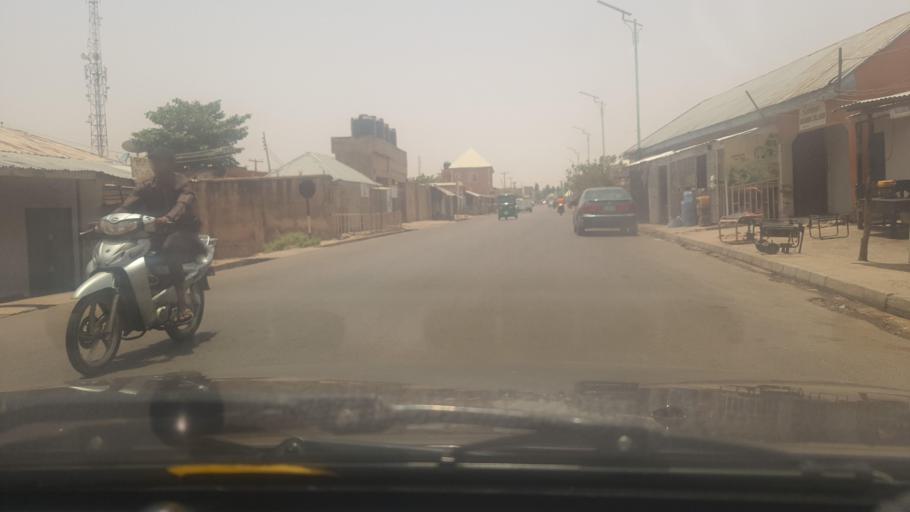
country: NG
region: Gombe
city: Gombe
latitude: 10.2988
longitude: 11.1510
